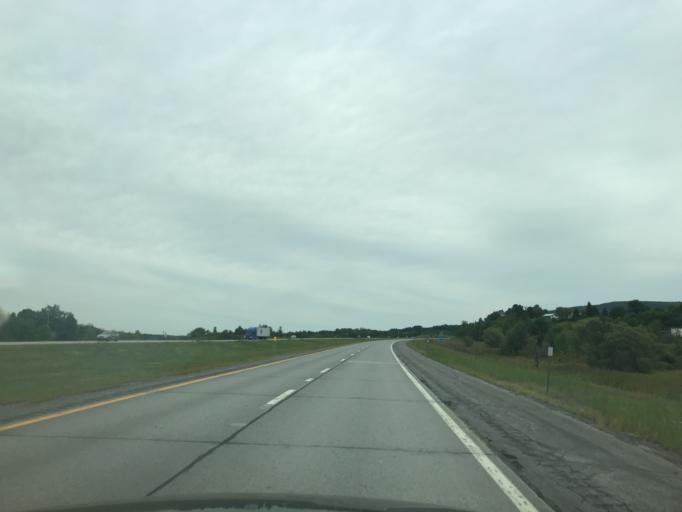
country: US
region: New York
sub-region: Schoharie County
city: Cobleskill
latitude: 42.6730
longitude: -74.4751
